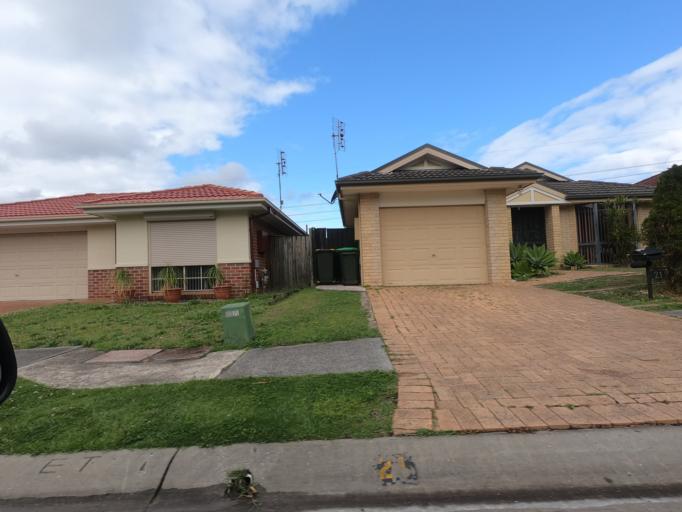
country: AU
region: New South Wales
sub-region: Wollongong
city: Dapto
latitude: -34.4881
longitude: 150.7676
